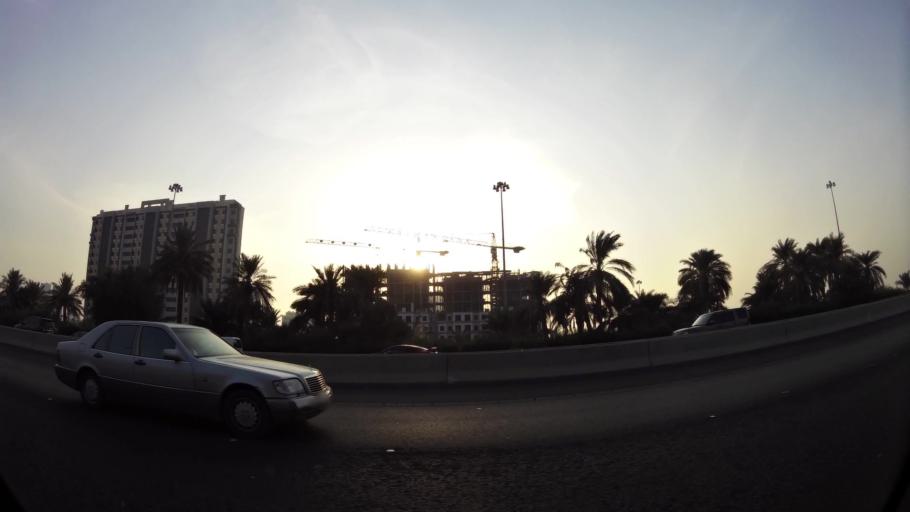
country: KW
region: Muhafazat Hawalli
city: Salwa
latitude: 29.2680
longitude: 48.0854
